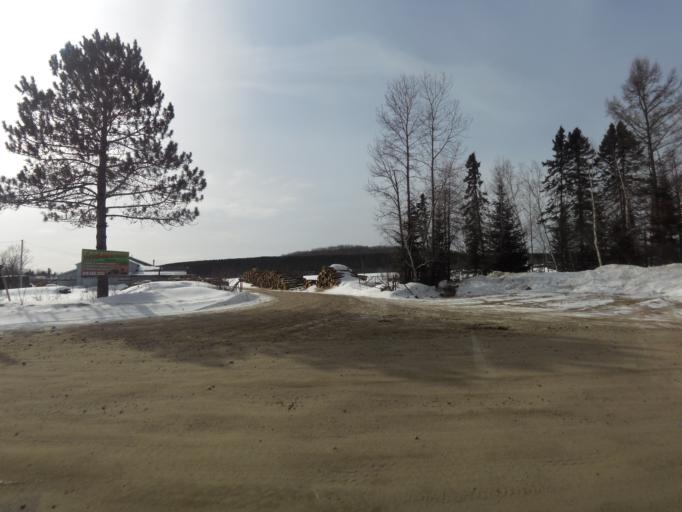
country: CA
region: Quebec
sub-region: Laurentides
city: Ferme-Neuve
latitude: 46.8863
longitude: -75.3286
